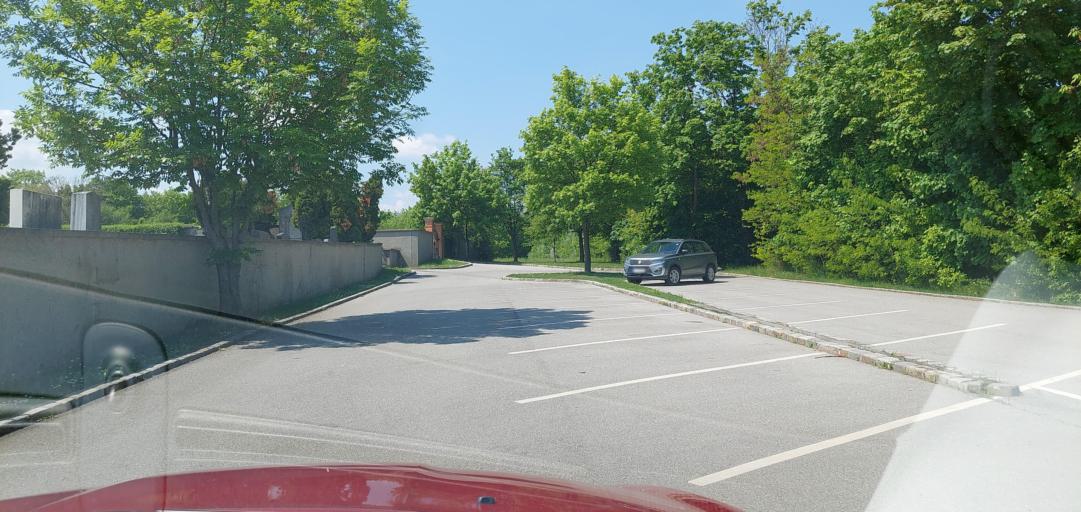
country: AT
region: Lower Austria
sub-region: Politischer Bezirk Bruck an der Leitha
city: Enzersdorf an der Fischa
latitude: 48.0865
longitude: 16.5984
